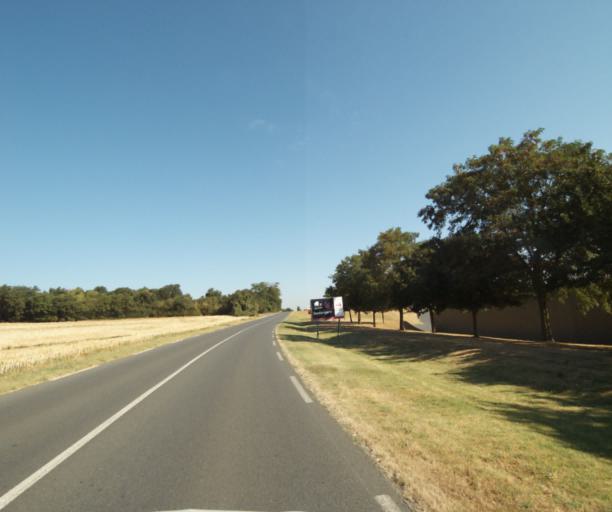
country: FR
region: Ile-de-France
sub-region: Departement de l'Essonne
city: Baulne
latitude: 48.4998
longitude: 2.3486
